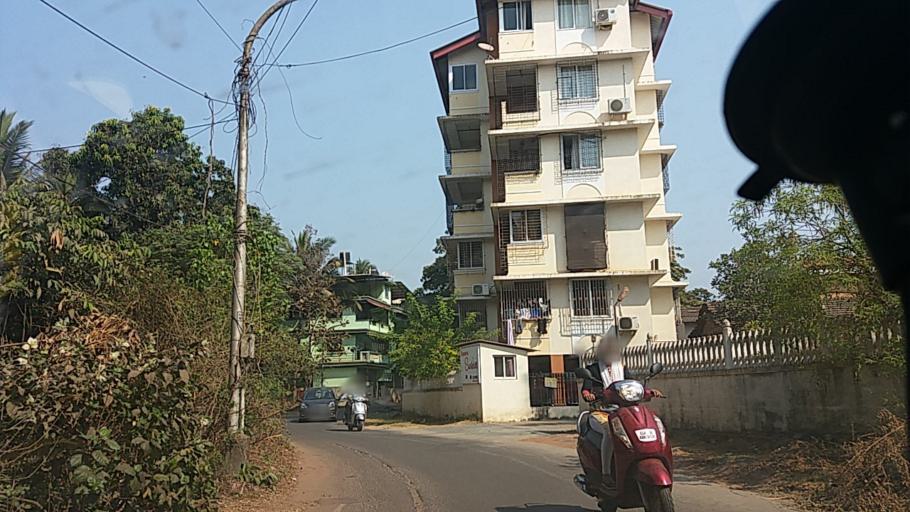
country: IN
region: Goa
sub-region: South Goa
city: Madgaon
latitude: 15.2827
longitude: 73.9542
